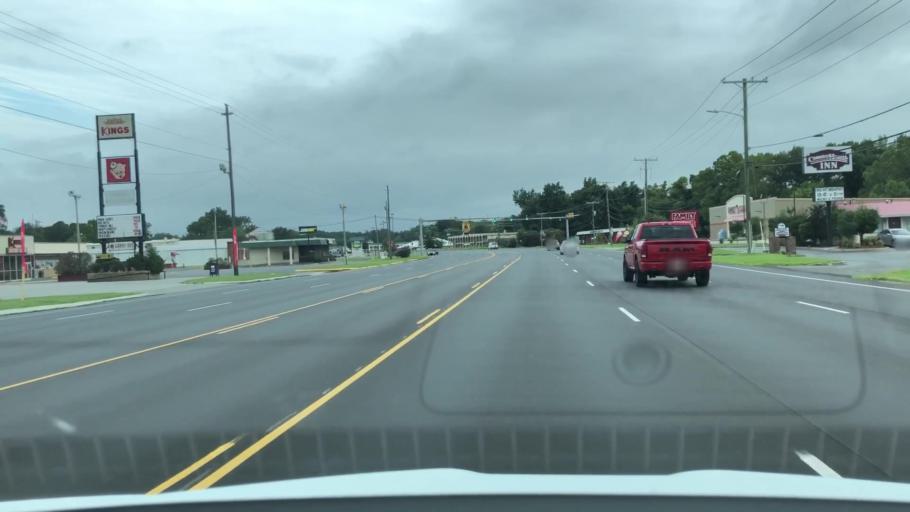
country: US
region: North Carolina
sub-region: Lenoir County
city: Kinston
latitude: 35.2412
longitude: -77.5777
